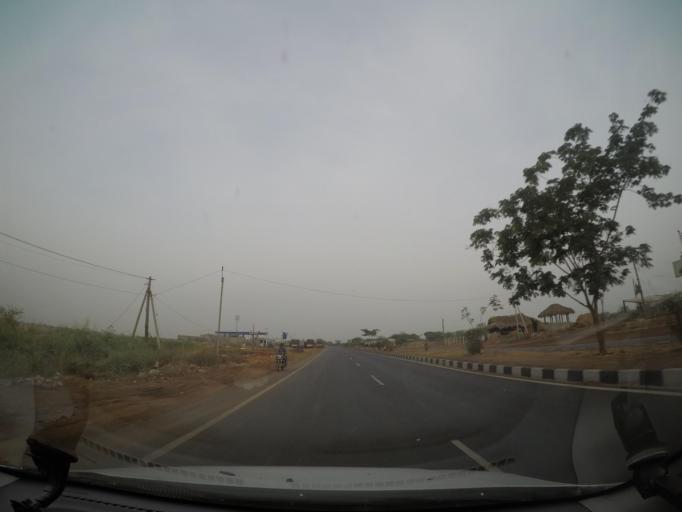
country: IN
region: Andhra Pradesh
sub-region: West Godavari
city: Eluru
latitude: 16.6320
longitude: 80.9536
